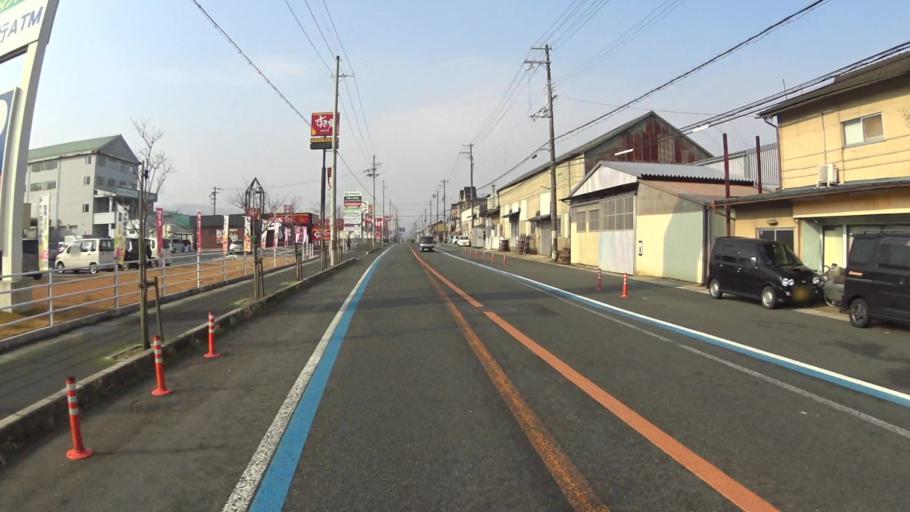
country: JP
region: Kyoto
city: Fukuchiyama
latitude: 35.2979
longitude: 135.1644
